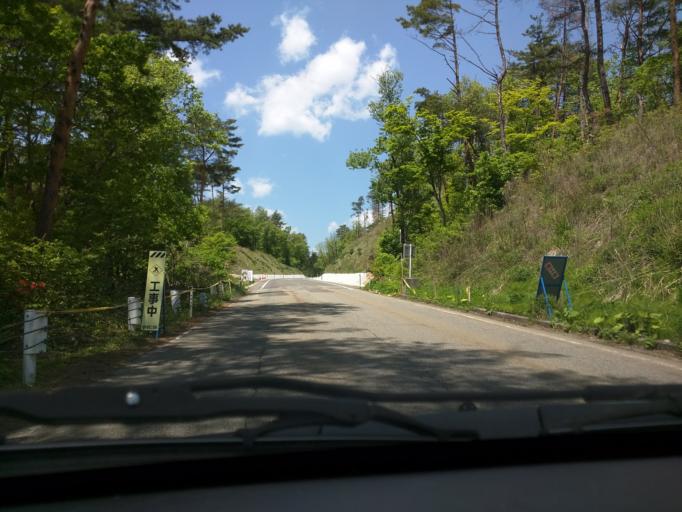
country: JP
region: Fukushima
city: Kitakata
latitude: 37.6333
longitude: 139.8268
